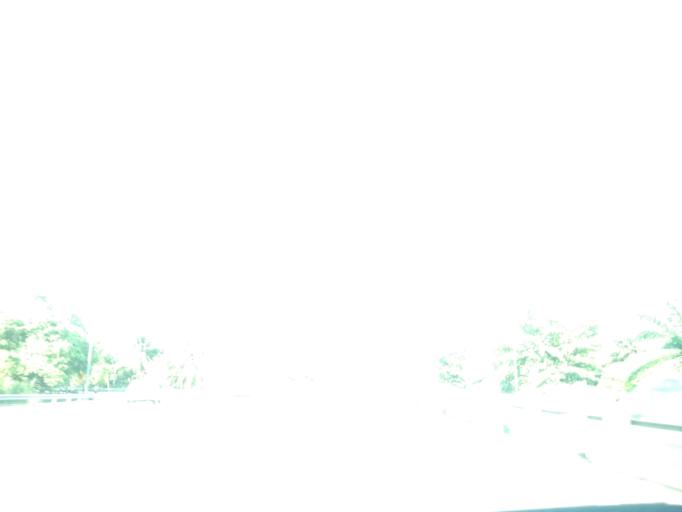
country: MY
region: Penang
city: Bukit Mertajam
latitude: 5.4058
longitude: 100.4844
